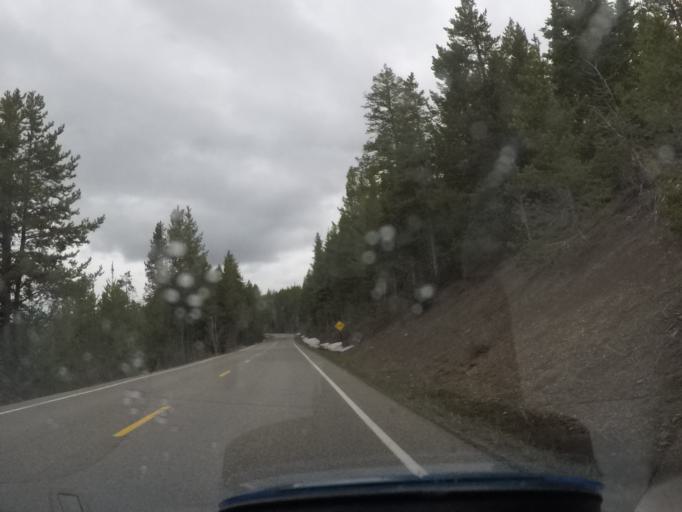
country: US
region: Wyoming
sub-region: Teton County
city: Moose Wilson Road
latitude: 43.9877
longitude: -110.6671
